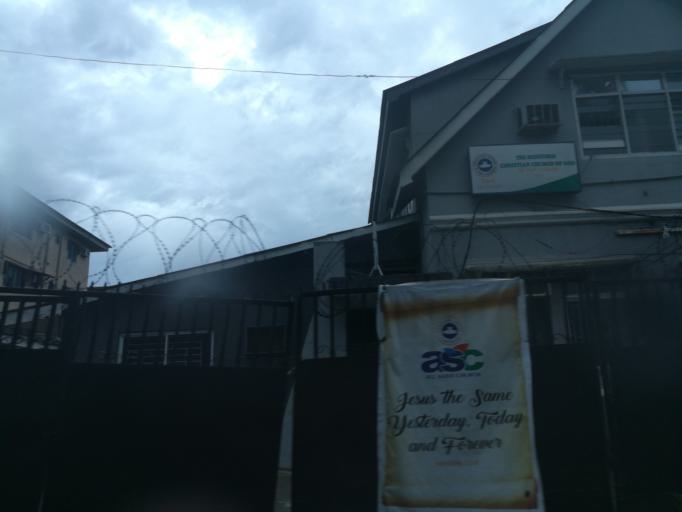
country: NG
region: Lagos
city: Makoko
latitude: 6.4972
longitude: 3.3780
